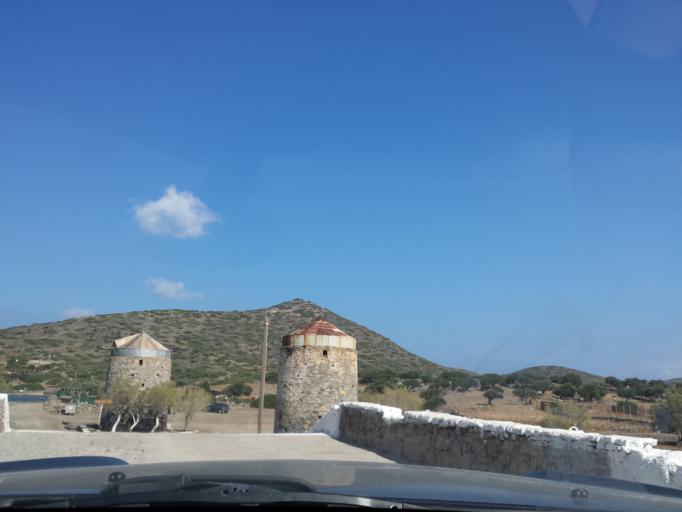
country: GR
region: Crete
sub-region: Nomos Lasithiou
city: Skhisma
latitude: 35.2573
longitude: 25.7352
